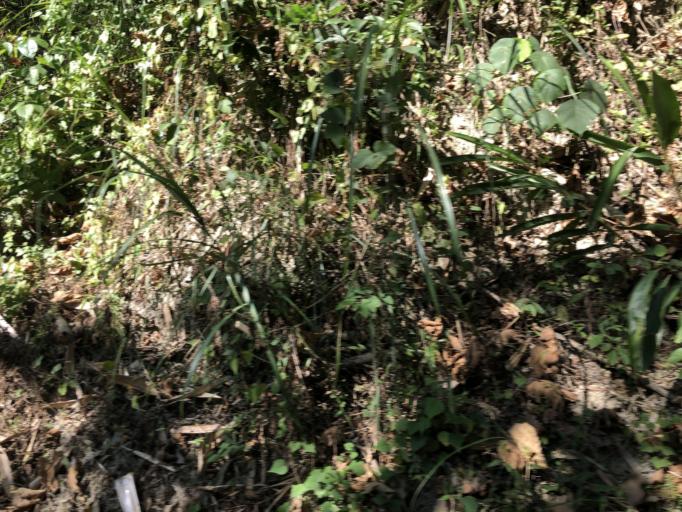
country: TW
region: Taiwan
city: Yujing
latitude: 23.0274
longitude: 120.3931
